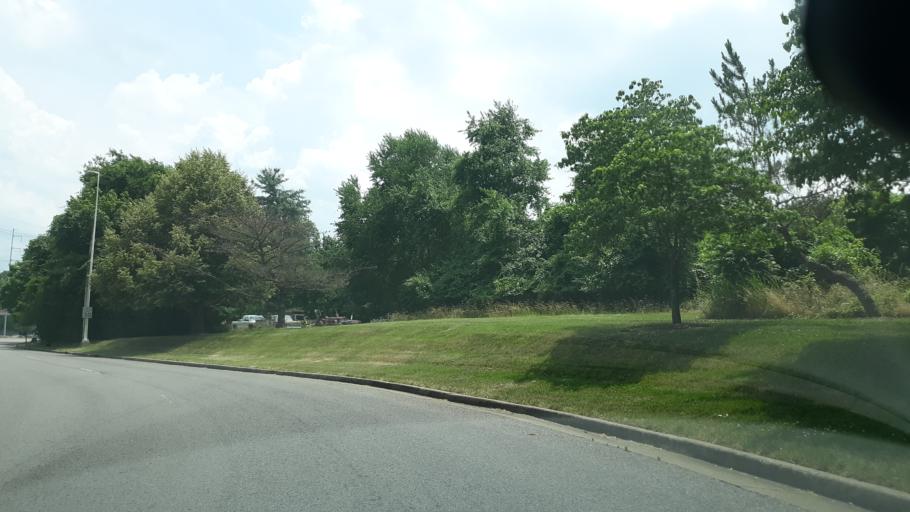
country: US
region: Tennessee
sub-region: Davidson County
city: Lakewood
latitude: 36.1817
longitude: -86.6082
